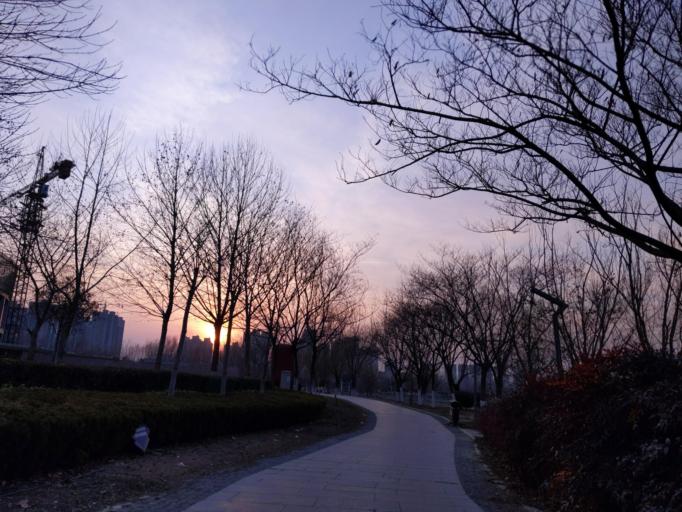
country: CN
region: Henan Sheng
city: Zhongyuanlu
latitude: 35.7767
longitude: 115.1292
